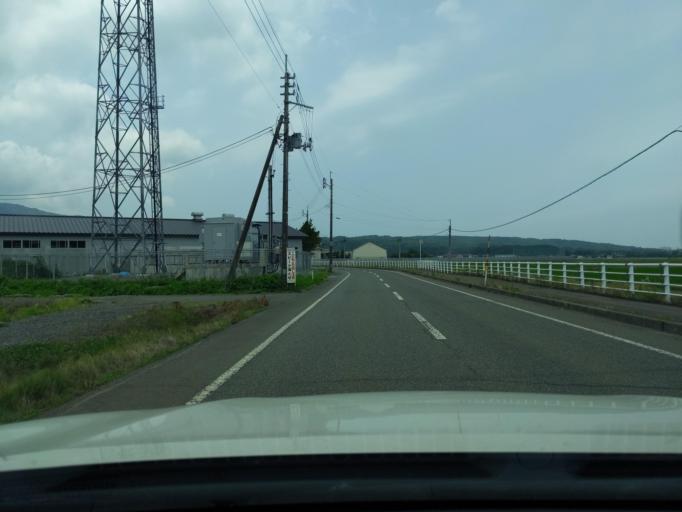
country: JP
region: Niigata
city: Kashiwazaki
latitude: 37.3301
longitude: 138.5717
